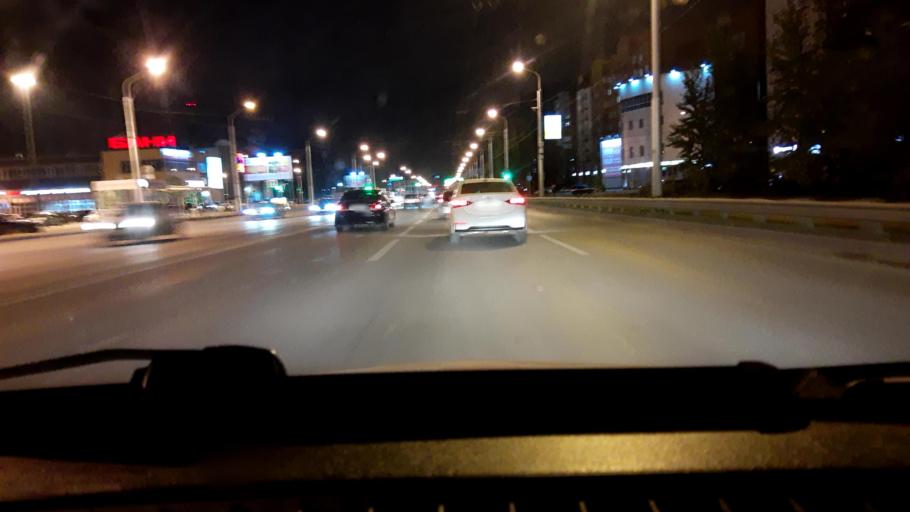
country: RU
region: Bashkortostan
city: Ufa
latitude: 54.7772
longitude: 56.0686
